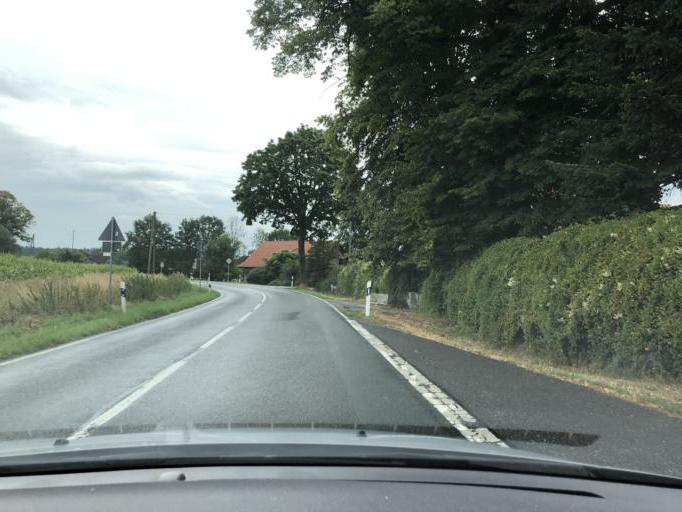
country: DE
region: North Rhine-Westphalia
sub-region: Regierungsbezirk Dusseldorf
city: Schermbeck
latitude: 51.6469
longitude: 6.8939
